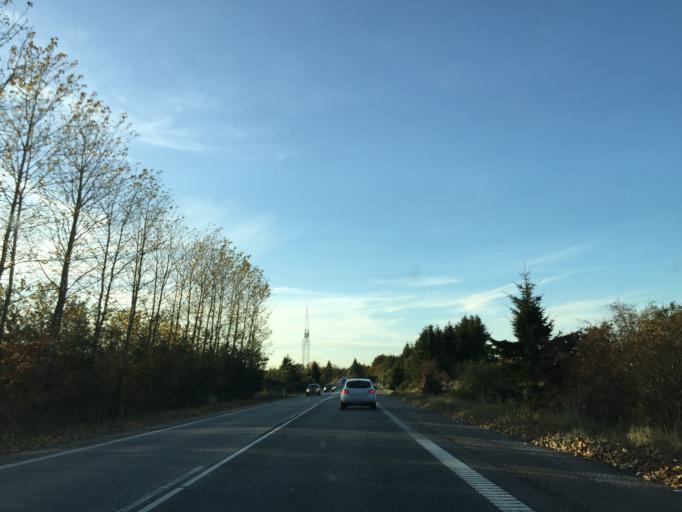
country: DK
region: South Denmark
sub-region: Aabenraa Kommune
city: Krusa
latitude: 54.8725
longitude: 9.3868
